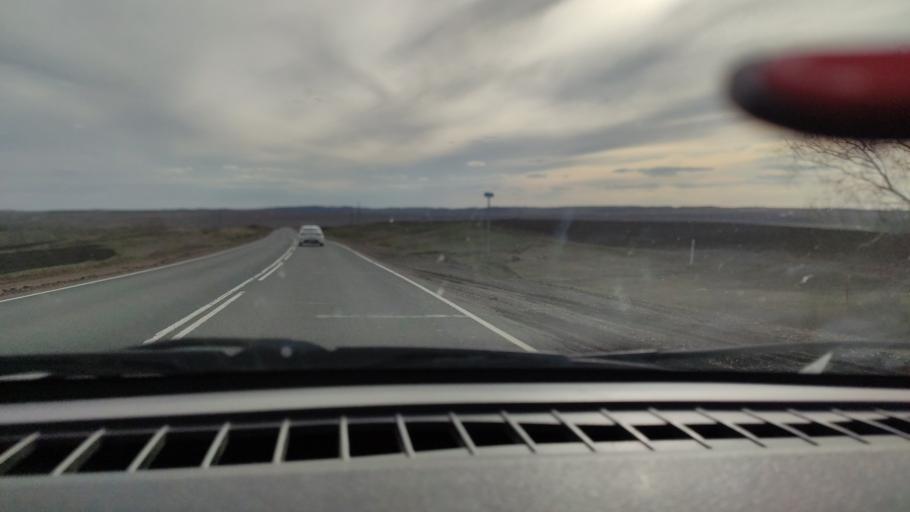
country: RU
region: Bashkortostan
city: Yermolayevo
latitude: 52.6755
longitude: 55.8502
